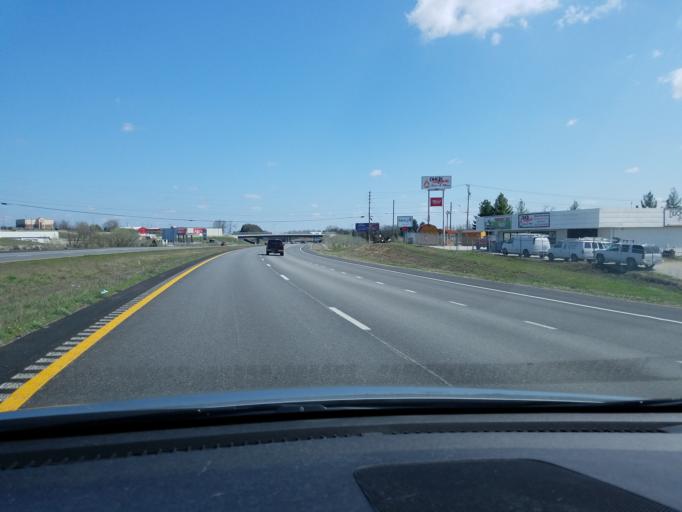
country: US
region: Missouri
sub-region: Taney County
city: Hollister
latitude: 36.6158
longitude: -93.2294
